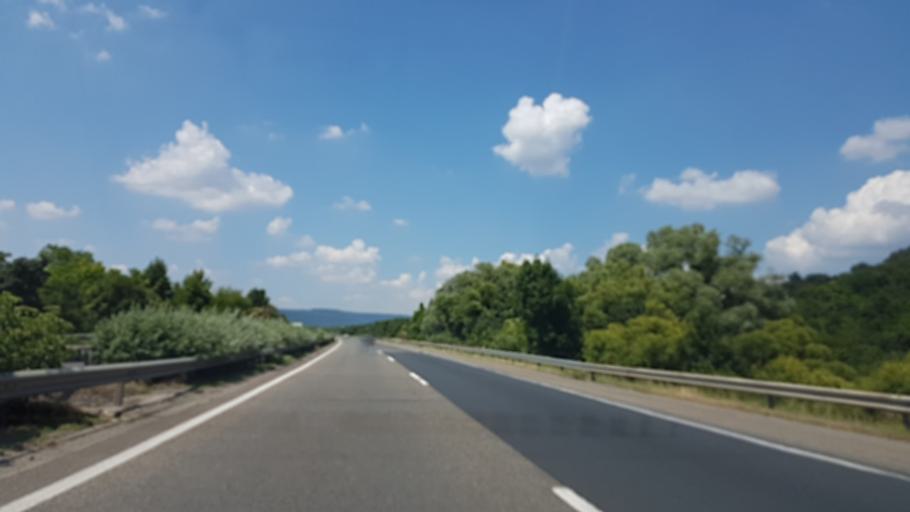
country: HU
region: Fejer
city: Szarliget
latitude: 47.5496
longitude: 18.4942
